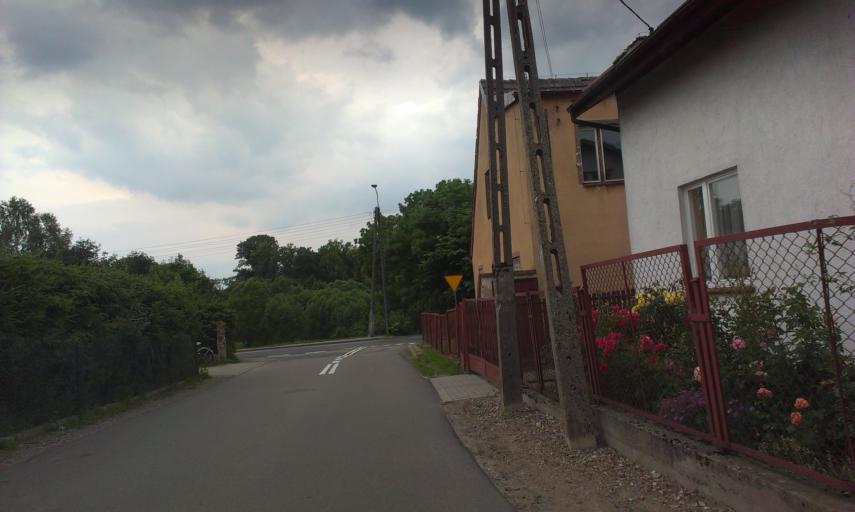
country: PL
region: West Pomeranian Voivodeship
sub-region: Powiat koszalinski
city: Bobolice
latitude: 53.8596
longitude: 16.6093
